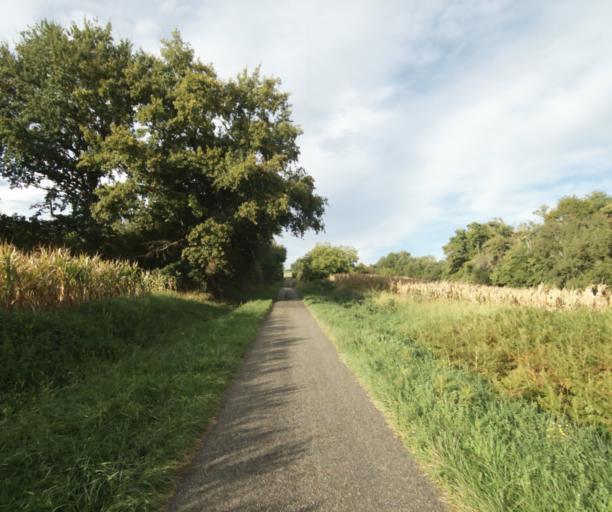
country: FR
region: Midi-Pyrenees
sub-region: Departement du Gers
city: Le Houga
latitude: 43.8598
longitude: -0.1552
